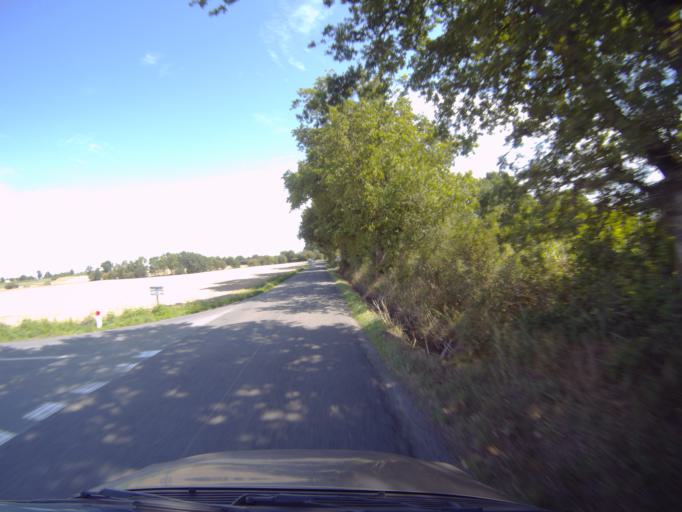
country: FR
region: Pays de la Loire
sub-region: Departement de la Loire-Atlantique
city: Saint-Hilaire-de-Clisson
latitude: 47.0754
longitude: -1.3095
